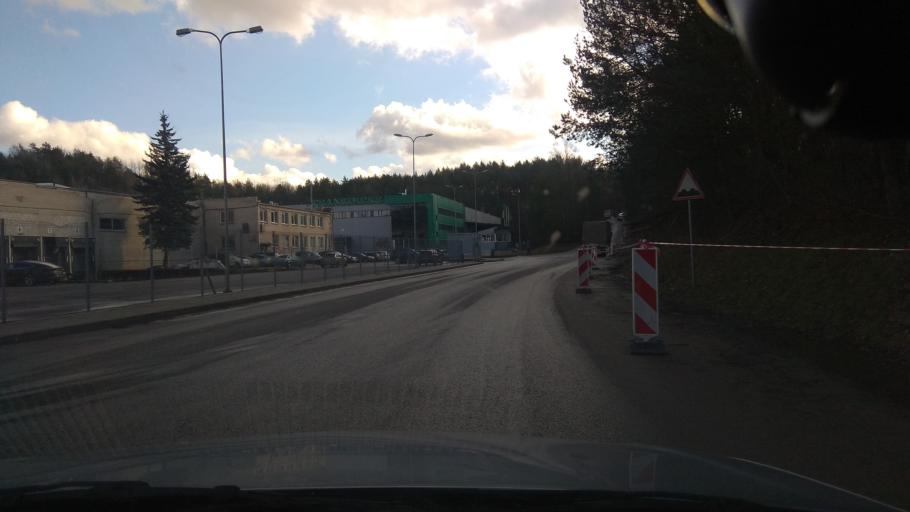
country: LT
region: Vilnius County
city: Lazdynai
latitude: 54.6442
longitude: 25.2217
